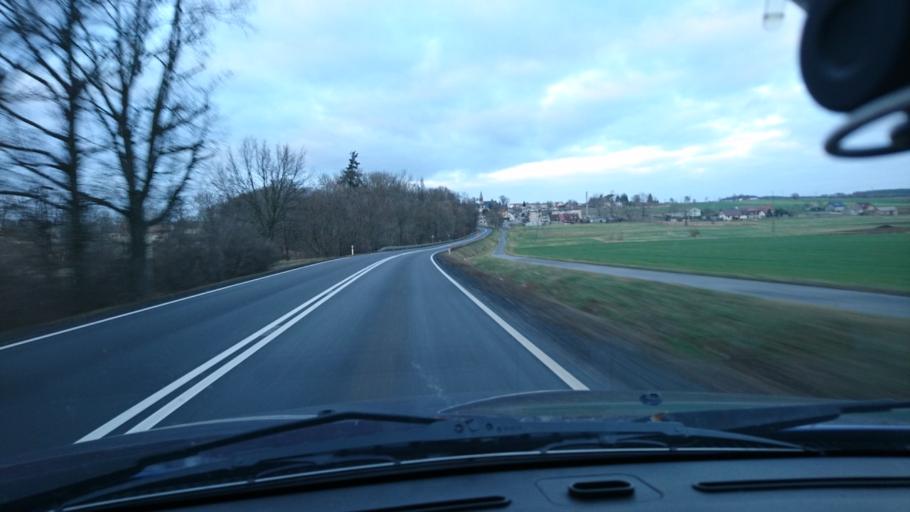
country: PL
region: Greater Poland Voivodeship
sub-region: Powiat ostrzeszowski
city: Ostrzeszow
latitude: 51.3804
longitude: 17.9465
